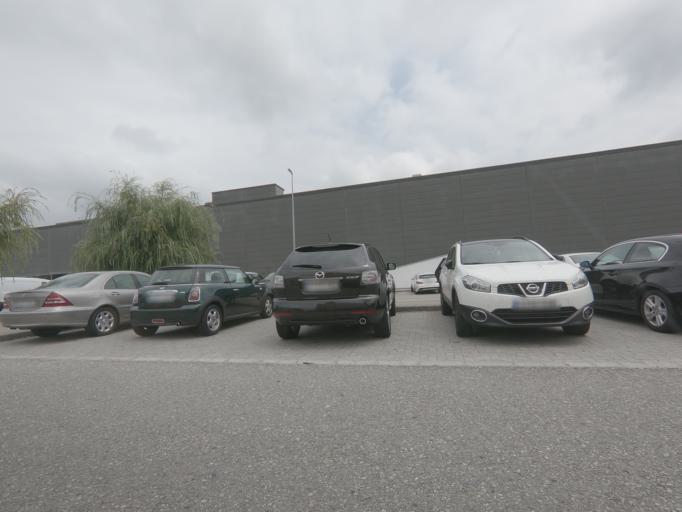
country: PT
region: Viana do Castelo
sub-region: Valenca
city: Valenca
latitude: 42.0404
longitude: -8.6616
